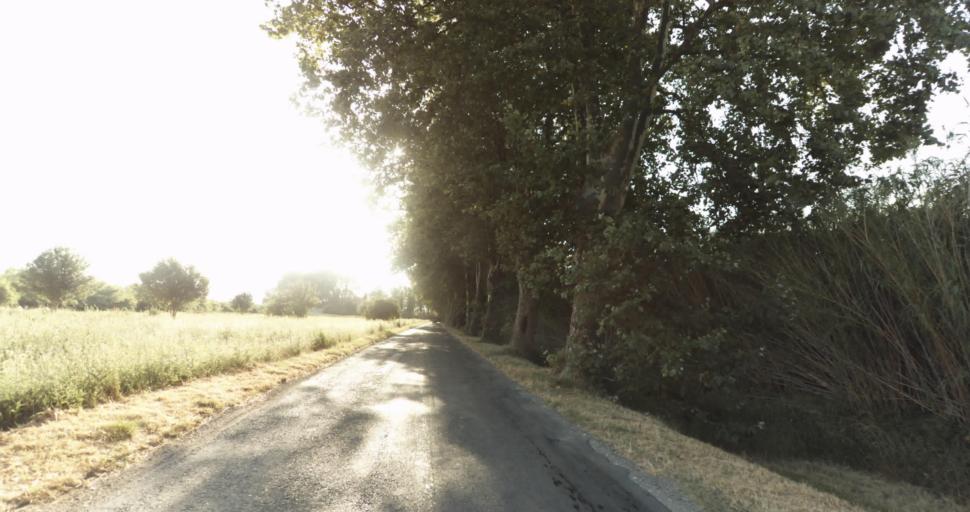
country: FR
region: Languedoc-Roussillon
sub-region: Departement des Pyrenees-Orientales
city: Latour-Bas-Elne
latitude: 42.5960
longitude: 3.0197
